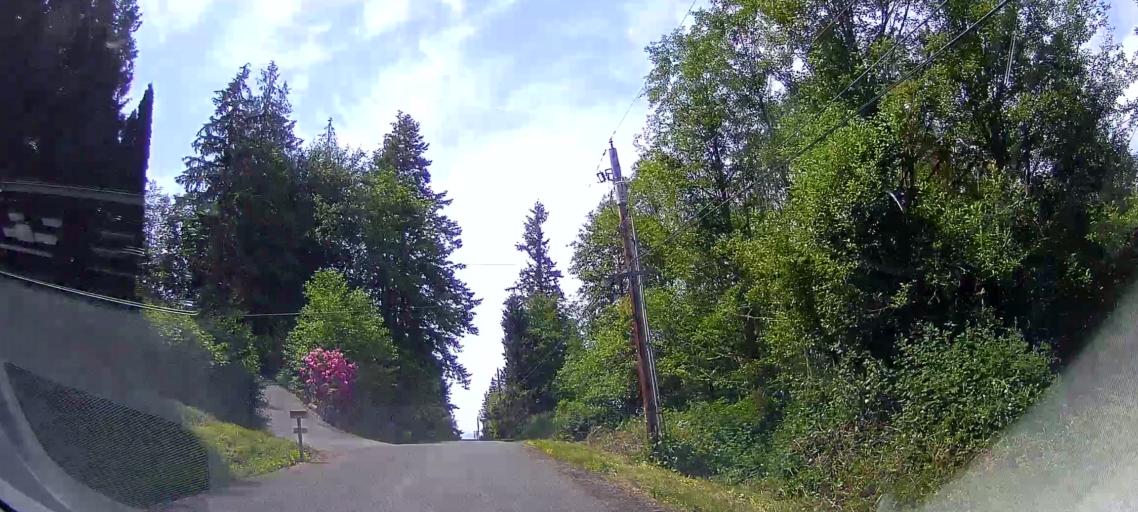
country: US
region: Washington
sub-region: Skagit County
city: Mount Vernon
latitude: 48.4064
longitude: -122.3023
